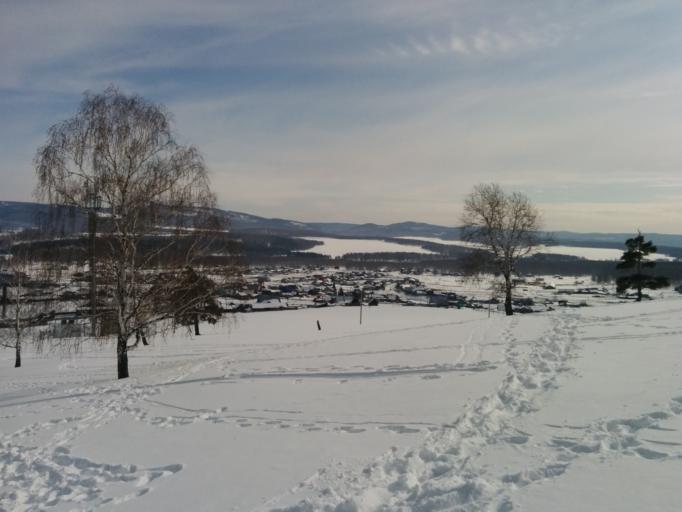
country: RU
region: Bashkortostan
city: Lomovka
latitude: 53.8082
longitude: 58.1942
